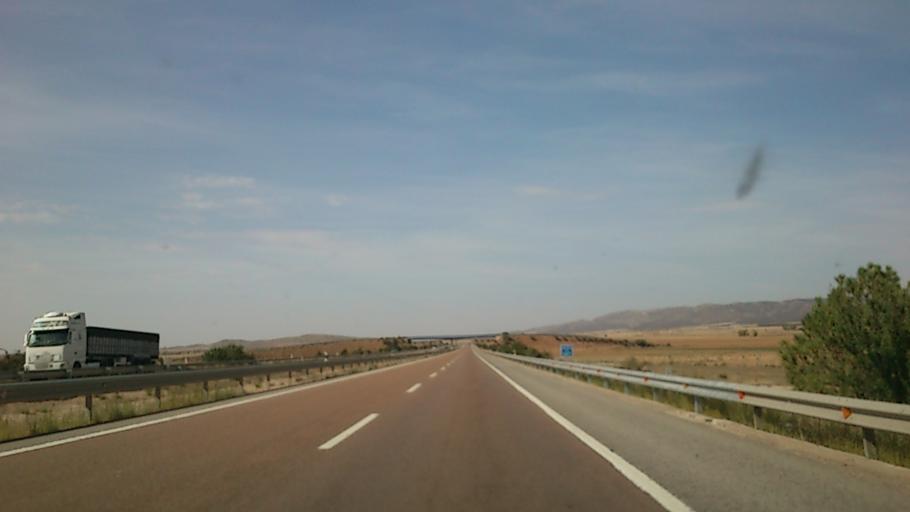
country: ES
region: Aragon
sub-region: Provincia de Teruel
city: Santa Eulalia
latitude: 40.5897
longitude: -1.2849
